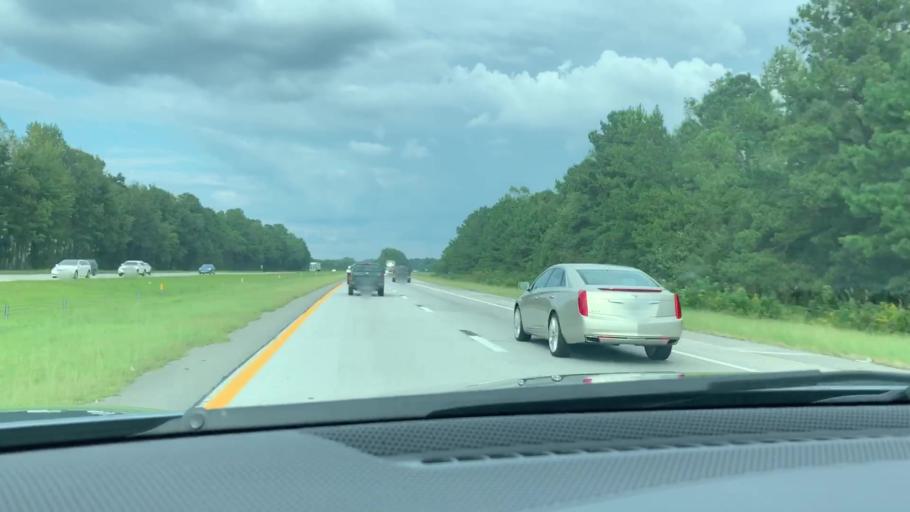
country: US
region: South Carolina
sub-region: Dorchester County
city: Saint George
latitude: 33.1329
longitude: -80.6358
